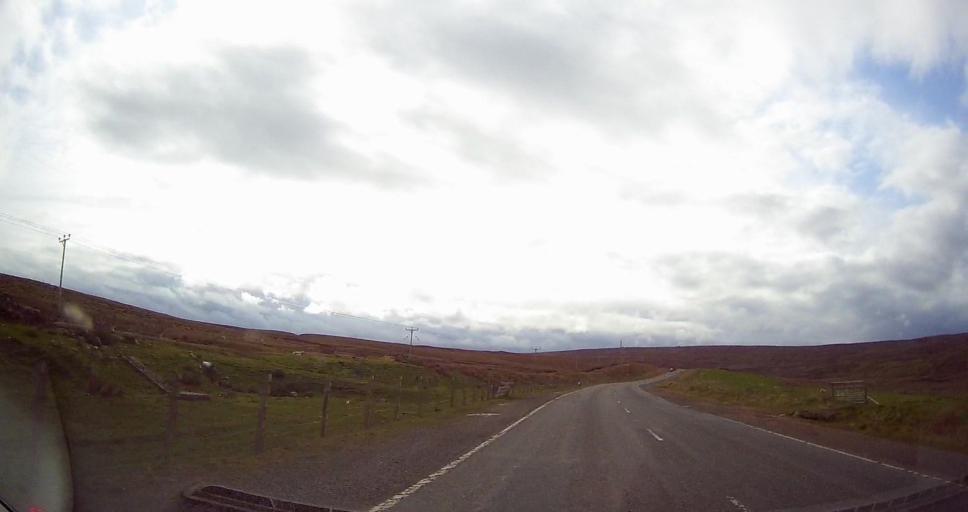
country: GB
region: Scotland
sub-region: Shetland Islands
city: Lerwick
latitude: 60.4442
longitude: -1.2395
